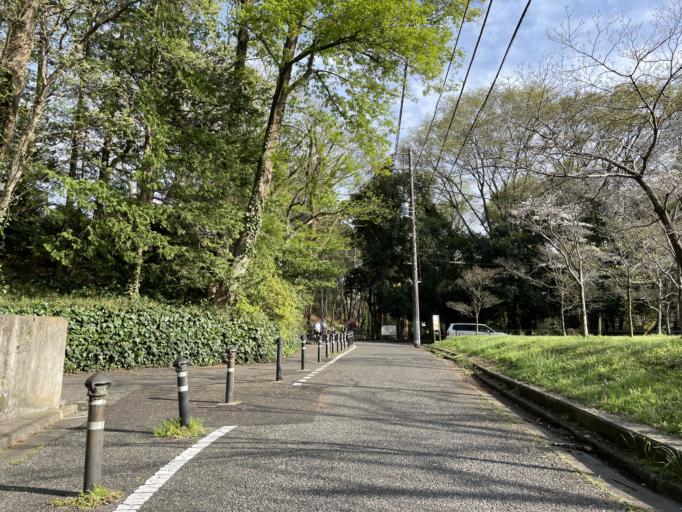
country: JP
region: Tokyo
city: Tokyo
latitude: 35.6862
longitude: 139.6398
